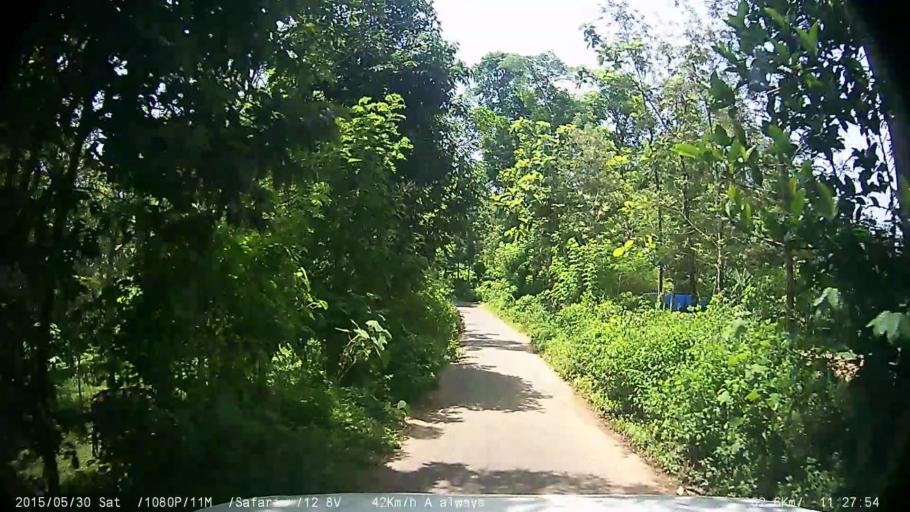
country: IN
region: Kerala
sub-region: Wayanad
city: Panamaram
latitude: 11.8122
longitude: 76.0428
